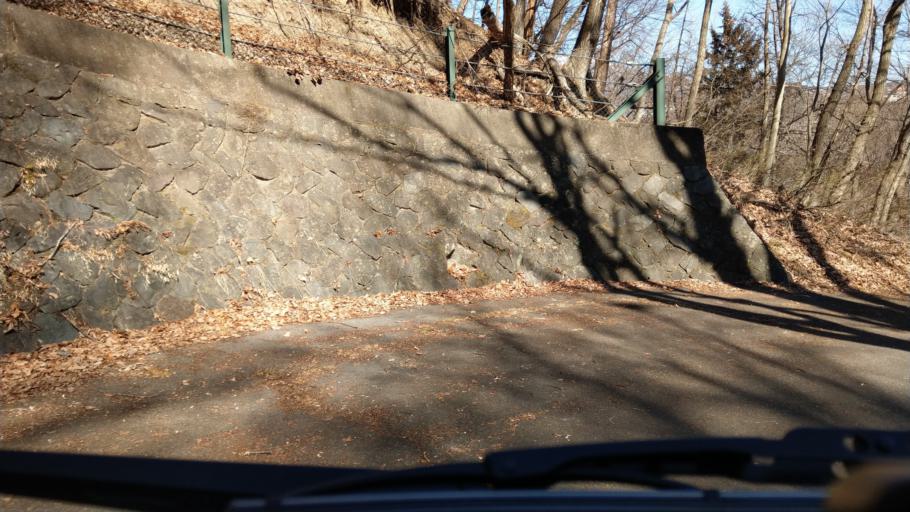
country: JP
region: Nagano
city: Komoro
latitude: 36.3228
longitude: 138.4093
